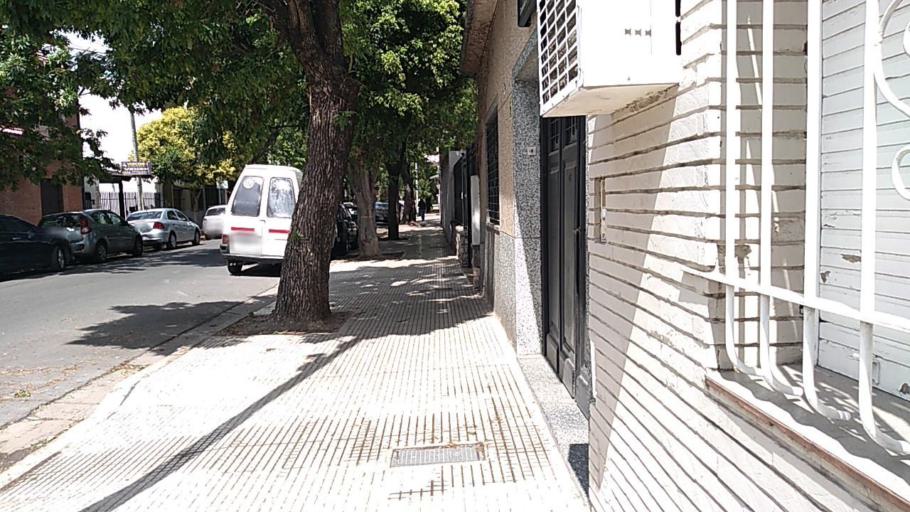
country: AR
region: Buenos Aires F.D.
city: Villa Santa Rita
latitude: -34.6145
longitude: -58.5167
